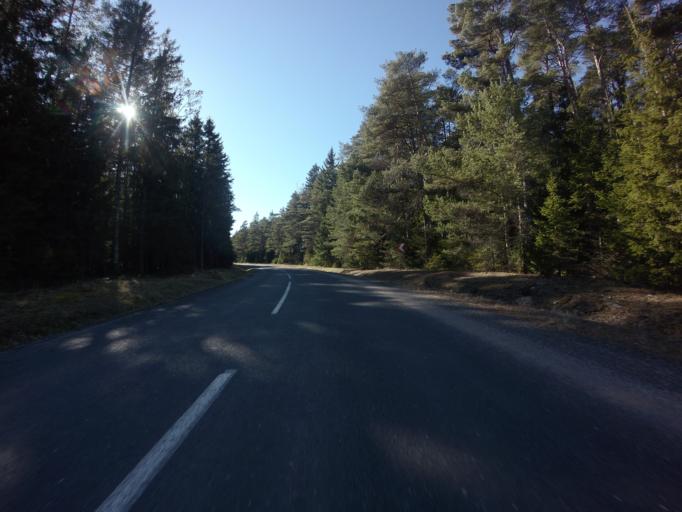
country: EE
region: Saare
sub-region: Kuressaare linn
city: Kuressaare
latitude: 58.5970
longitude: 22.5916
